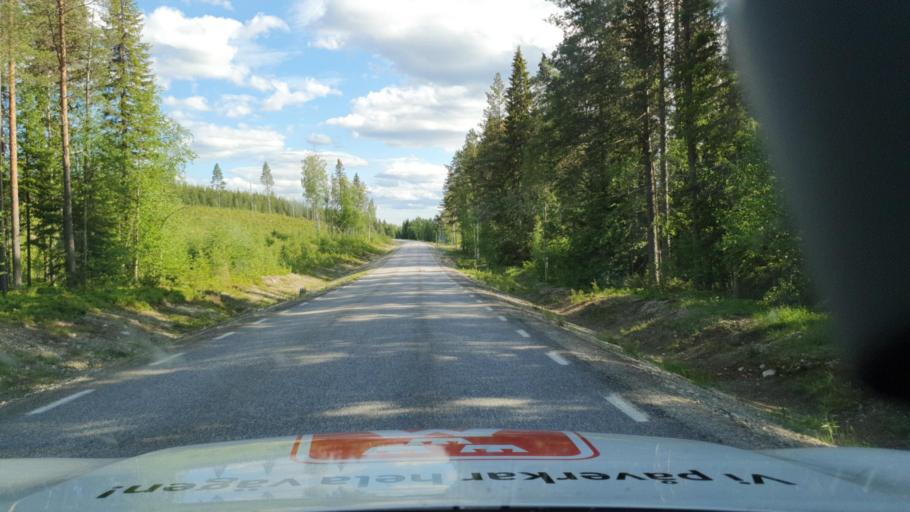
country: SE
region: Vaesterbotten
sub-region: Skelleftea Kommun
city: Langsele
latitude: 64.7334
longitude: 19.9536
